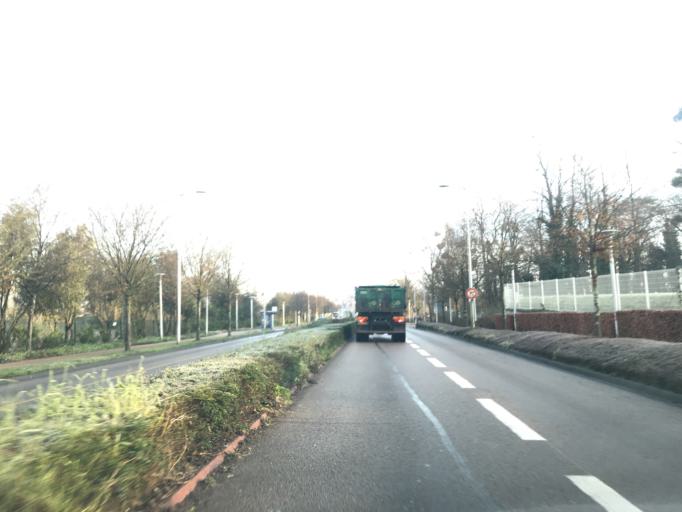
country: FR
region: Haute-Normandie
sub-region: Departement de la Seine-Maritime
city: Le Petit-Quevilly
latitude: 49.4042
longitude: 1.0669
